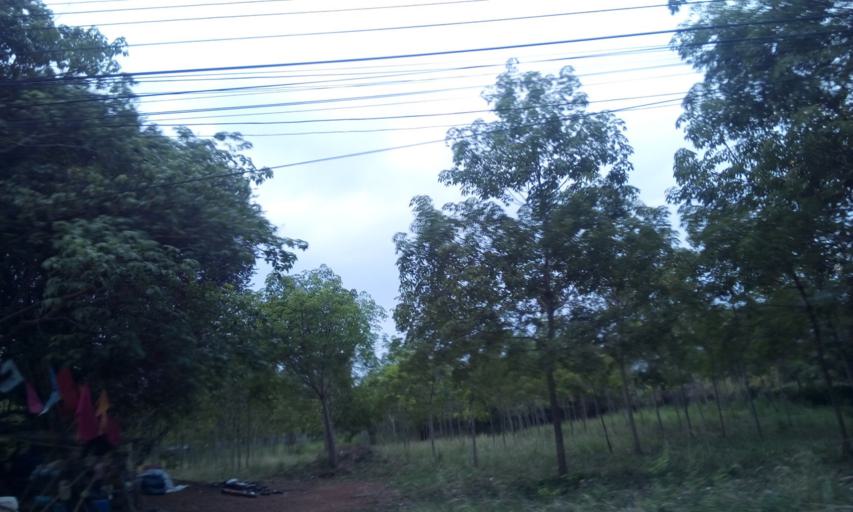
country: TH
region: Trat
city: Laem Ngop
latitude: 12.1898
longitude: 102.2961
